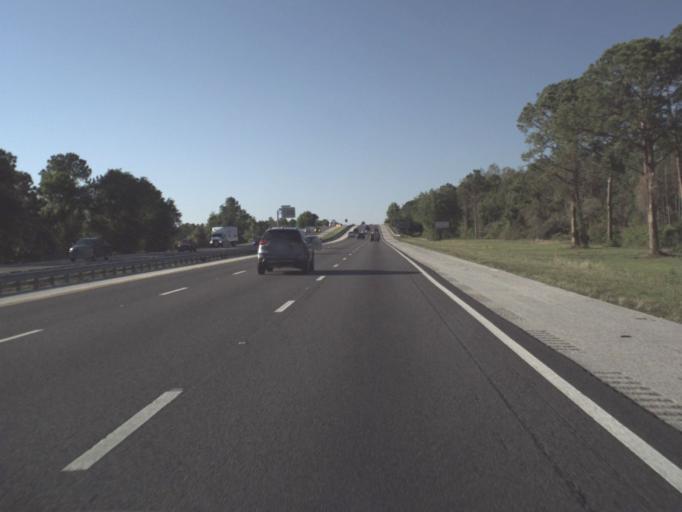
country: US
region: Florida
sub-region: Flagler County
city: Flagler Beach
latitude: 29.4914
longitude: -81.1895
